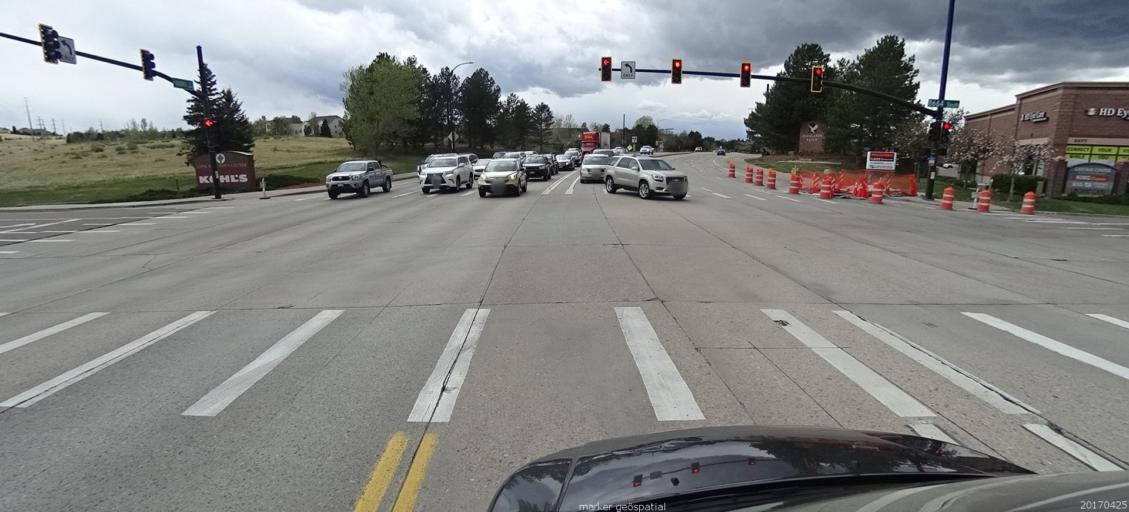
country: US
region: Colorado
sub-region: Douglas County
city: Acres Green
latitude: 39.5587
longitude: -104.9053
